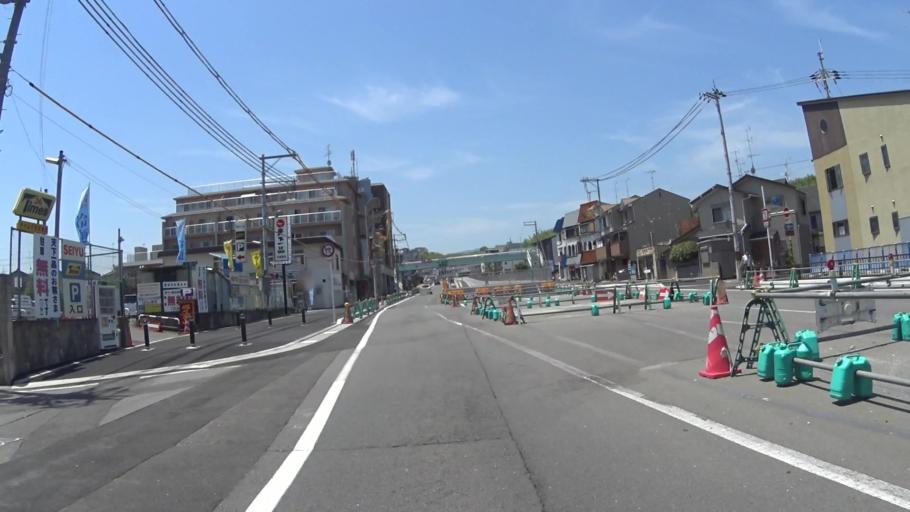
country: JP
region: Kyoto
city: Muko
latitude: 34.9802
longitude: 135.6911
